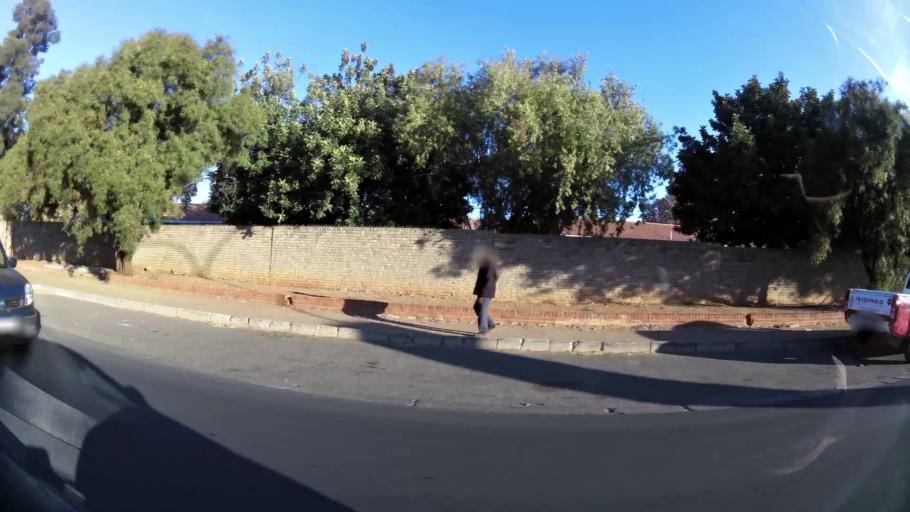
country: ZA
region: Northern Cape
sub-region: Frances Baard District Municipality
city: Kimberley
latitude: -28.7440
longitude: 24.7605
